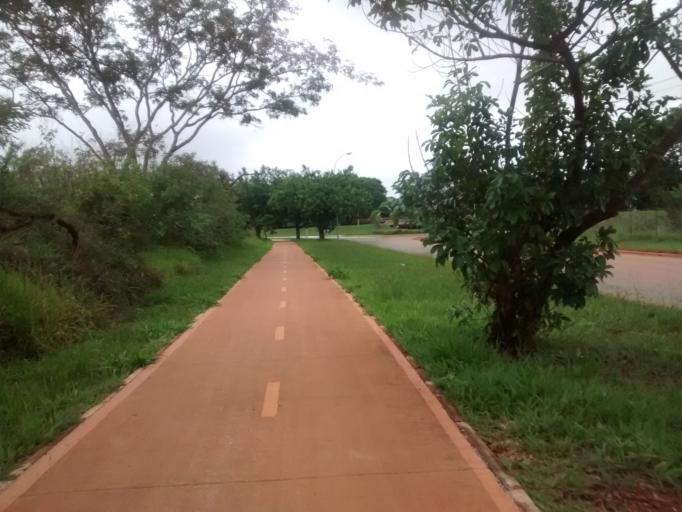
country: BR
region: Federal District
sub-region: Brasilia
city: Brasilia
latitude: -15.8034
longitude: -47.8493
